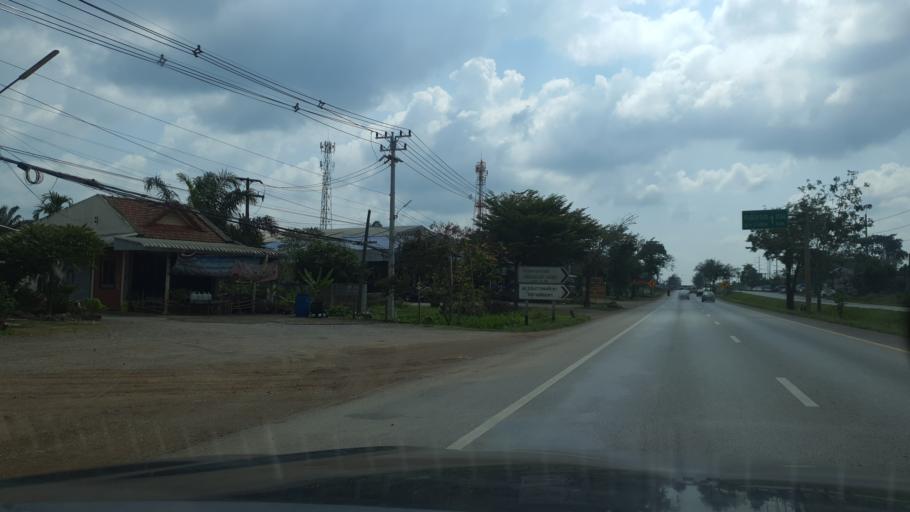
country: TH
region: Chumphon
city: Chumphon
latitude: 10.4618
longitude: 99.1313
